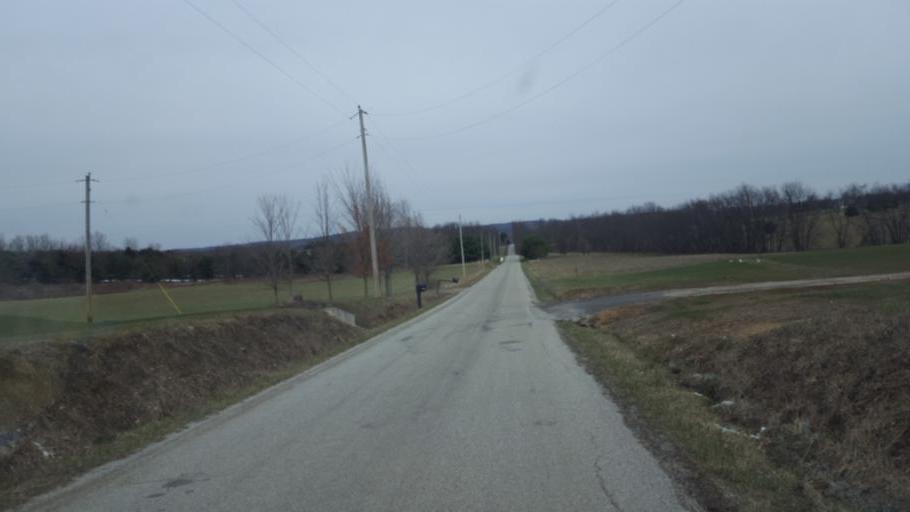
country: US
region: Ohio
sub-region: Sandusky County
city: Bellville
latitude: 40.5970
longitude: -82.5678
